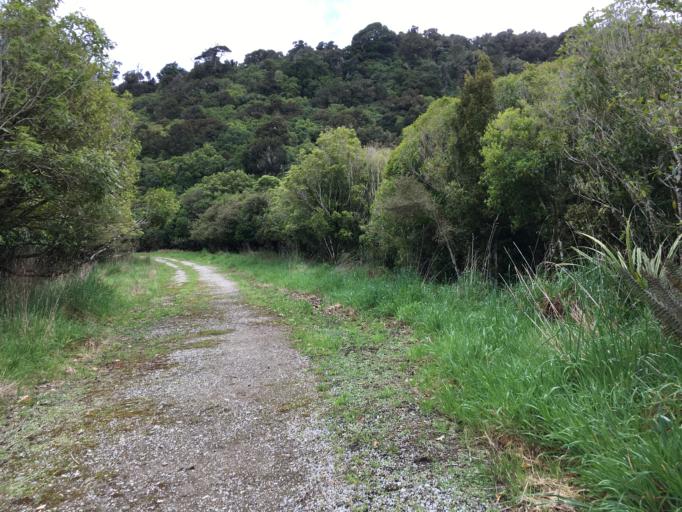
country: NZ
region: Otago
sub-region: Clutha District
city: Papatowai
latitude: -46.5039
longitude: 169.4846
